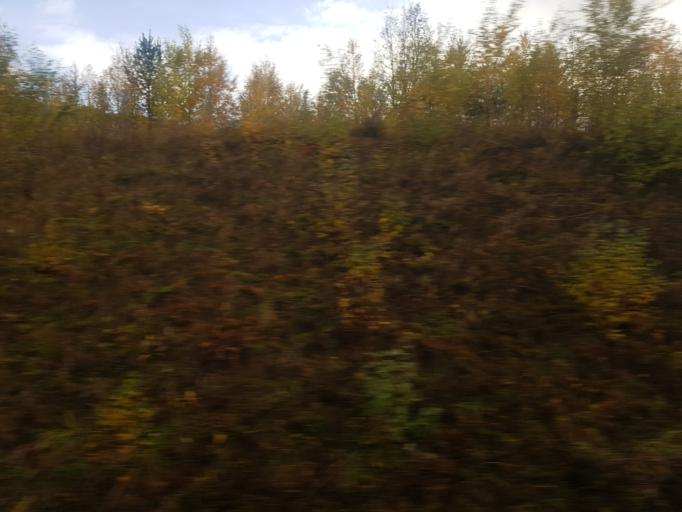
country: NO
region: Oppland
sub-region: Dovre
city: Dovre
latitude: 61.9669
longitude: 9.2598
